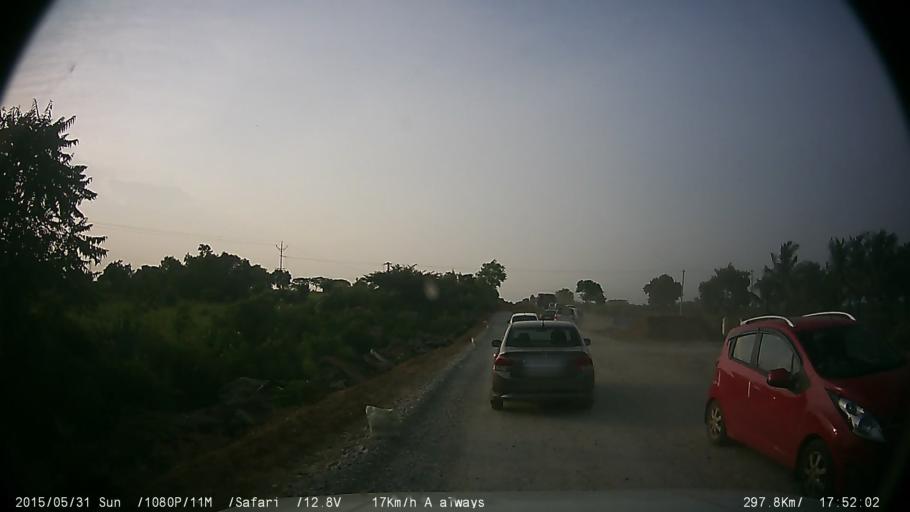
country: IN
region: Karnataka
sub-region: Mysore
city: Nanjangud
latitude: 11.9796
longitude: 76.6694
